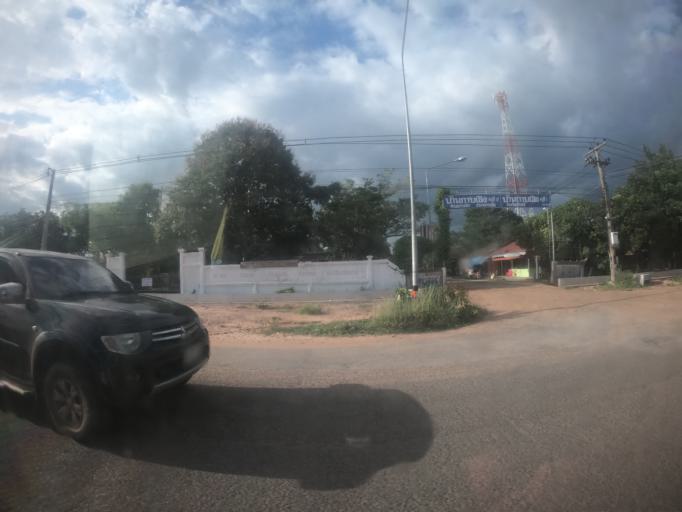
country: TH
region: Surin
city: Kap Choeng
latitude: 14.4748
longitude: 103.5994
